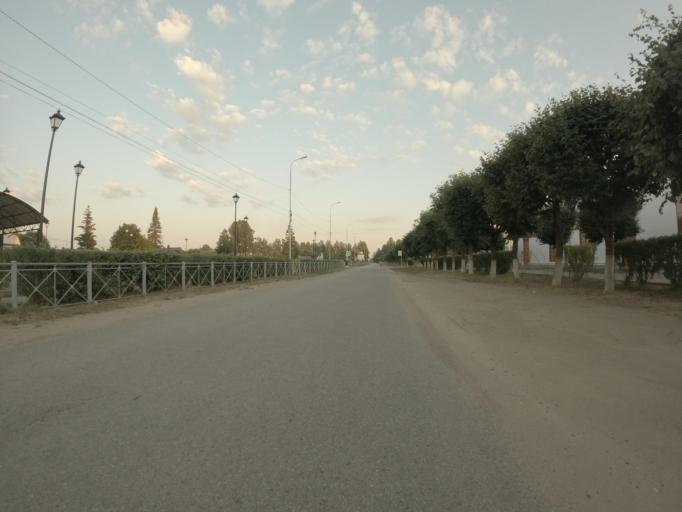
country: RU
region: Leningrad
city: Pavlovo
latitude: 59.8449
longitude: 30.9368
